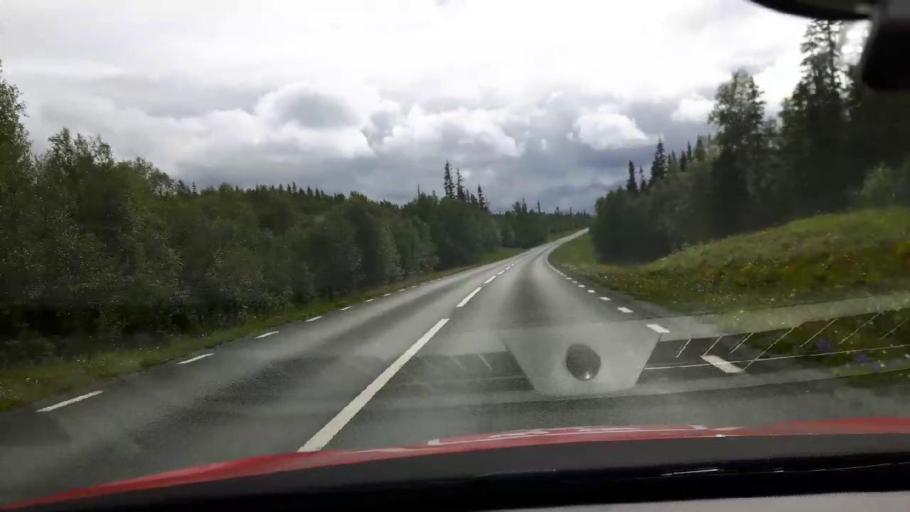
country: NO
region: Nord-Trondelag
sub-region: Meraker
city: Meraker
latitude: 63.2817
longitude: 12.3109
